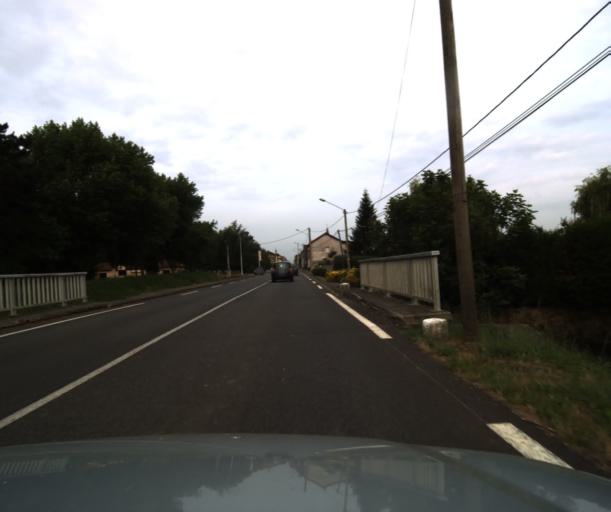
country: FR
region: Midi-Pyrenees
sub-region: Departement des Hautes-Pyrenees
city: Rabastens-de-Bigorre
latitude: 43.3888
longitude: 0.1564
